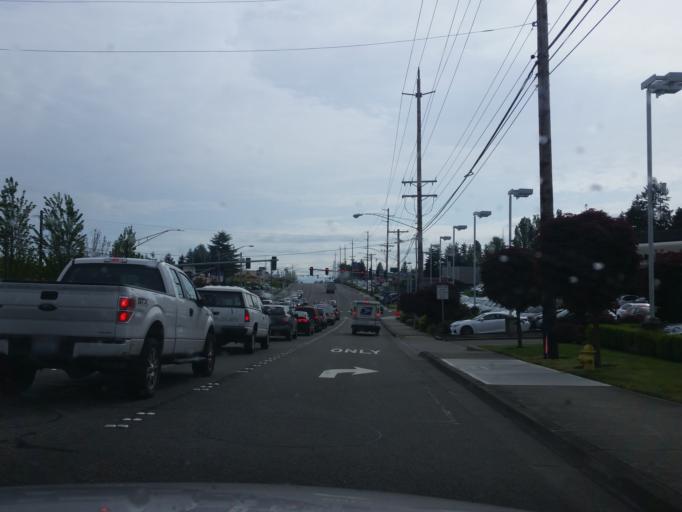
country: US
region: Washington
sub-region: Snohomish County
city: Lynnwood
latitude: 47.8150
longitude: -122.3207
